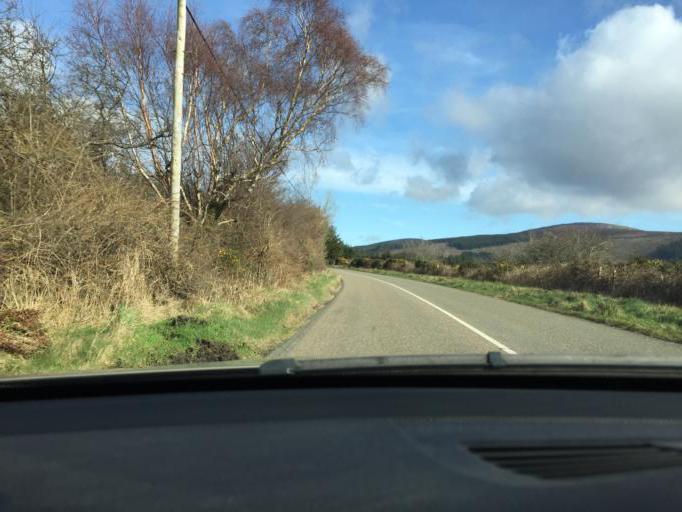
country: IE
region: Leinster
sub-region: Wicklow
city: Valleymount
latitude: 53.0600
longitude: -6.4814
